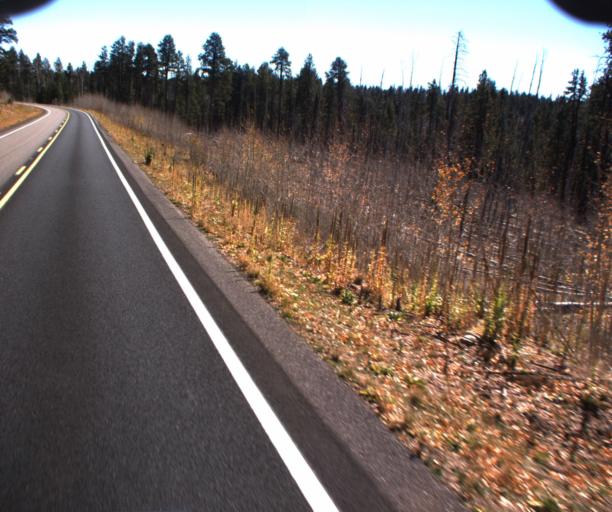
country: US
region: Arizona
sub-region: Coconino County
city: Grand Canyon
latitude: 36.5448
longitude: -112.1776
